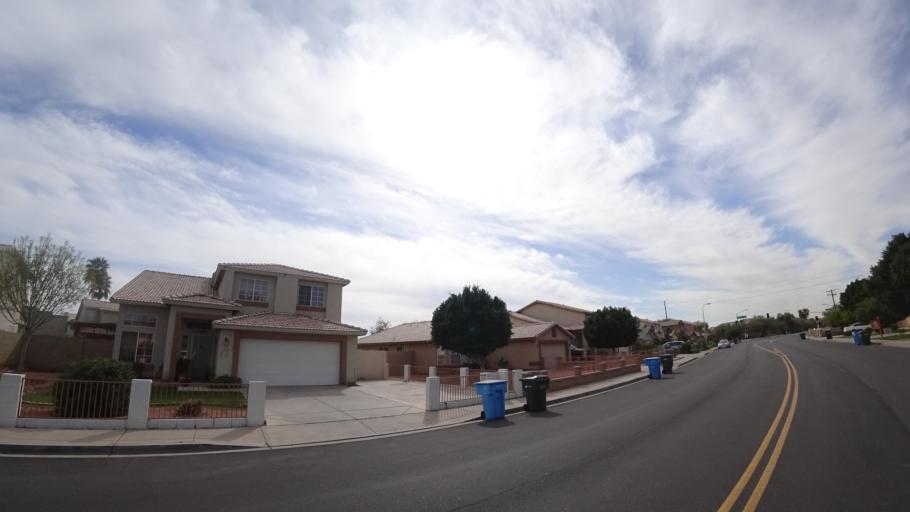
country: US
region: Arizona
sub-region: Maricopa County
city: Tolleson
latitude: 33.4724
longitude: -112.2538
